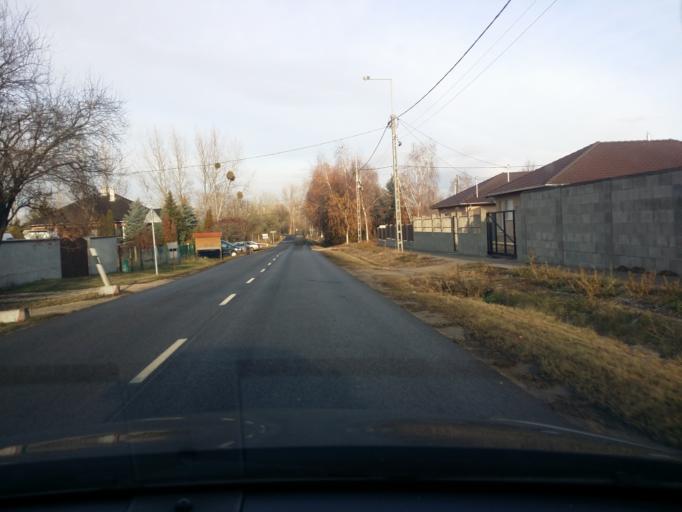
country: HU
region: Pest
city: Alsonemedi
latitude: 47.3275
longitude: 19.1452
